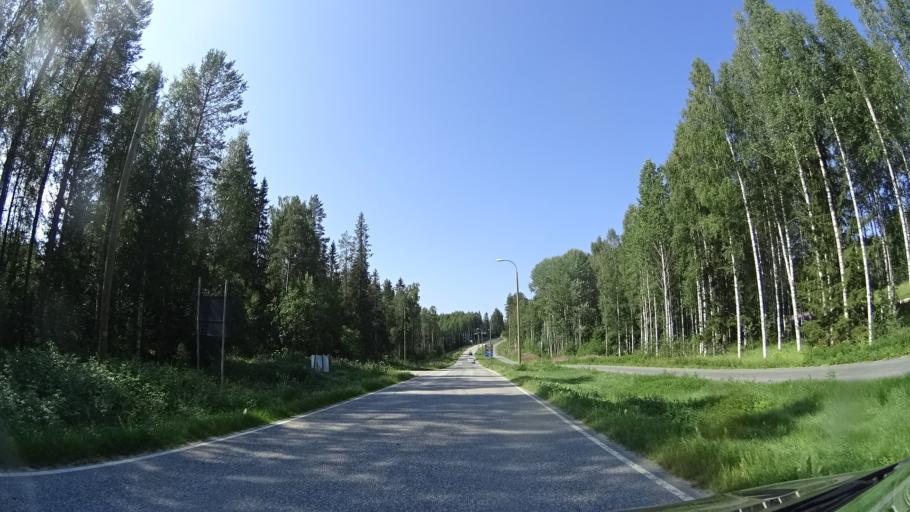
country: FI
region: North Karelia
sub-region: Pielisen Karjala
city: Lieksa
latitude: 63.1169
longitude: 29.7858
